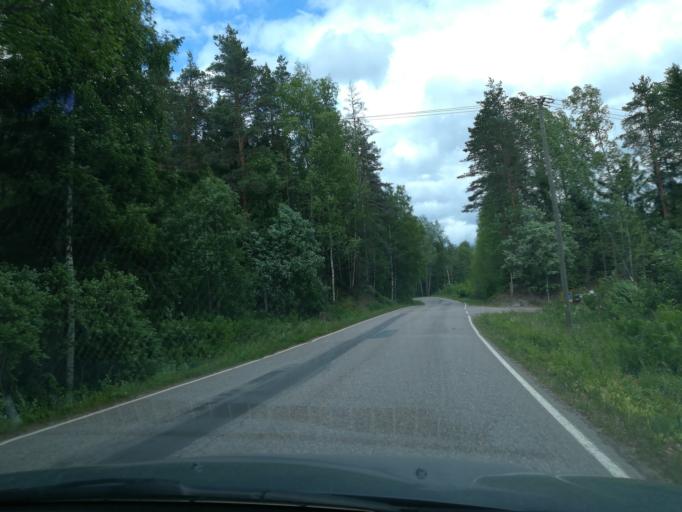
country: FI
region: South Karelia
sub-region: Lappeenranta
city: Savitaipale
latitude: 61.2238
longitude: 27.7039
